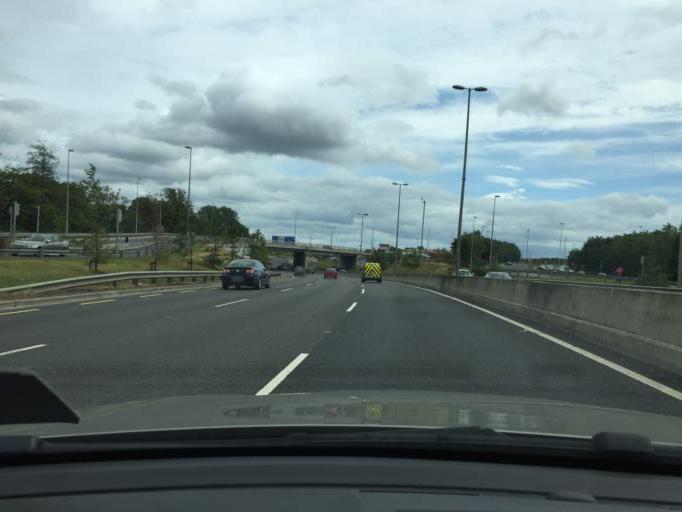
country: IE
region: Leinster
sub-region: Fingal County
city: Blanchardstown
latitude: 53.3856
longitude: -6.3690
